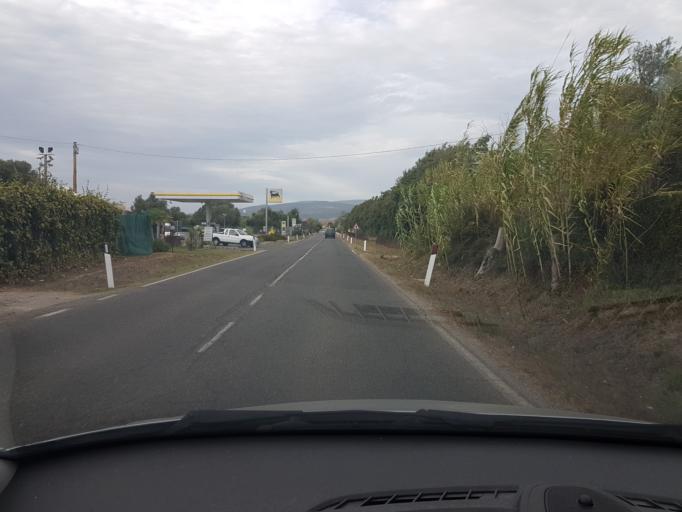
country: IT
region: Sardinia
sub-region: Provincia di Oristano
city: Nurachi
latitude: 39.9837
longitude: 8.5397
